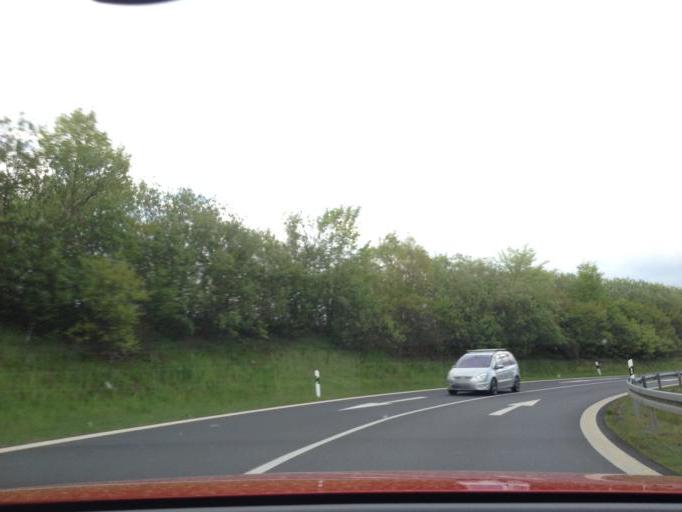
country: DE
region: Bavaria
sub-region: Upper Franconia
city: Marktredwitz
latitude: 50.0180
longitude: 12.1128
